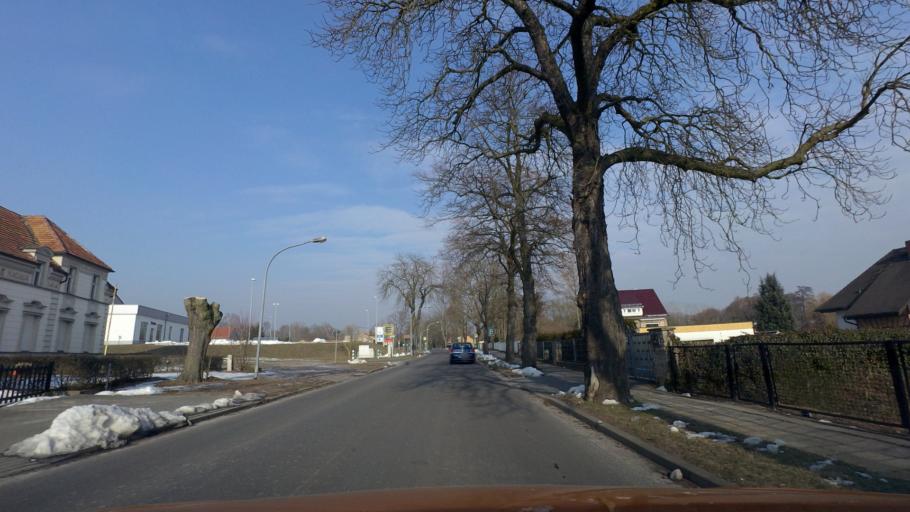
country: DE
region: Brandenburg
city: Am Mellensee
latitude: 52.1599
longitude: 13.4029
